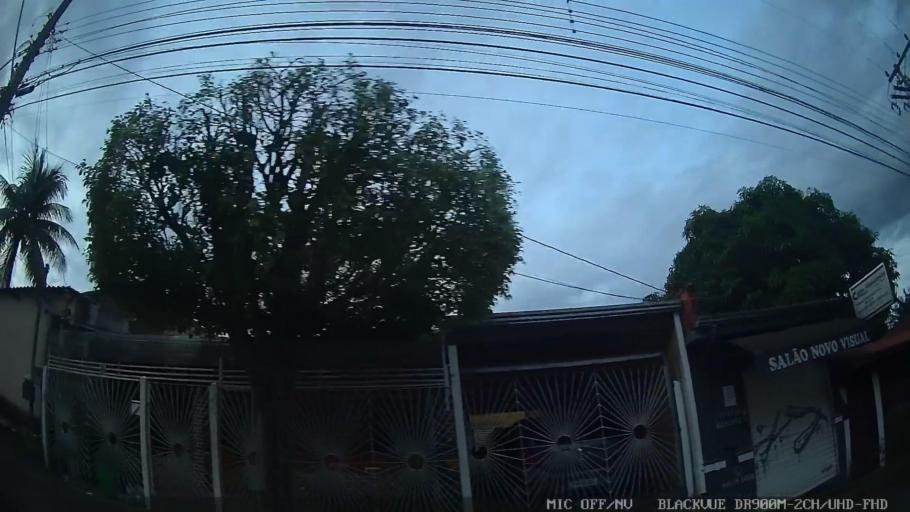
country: BR
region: Sao Paulo
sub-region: Indaiatuba
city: Indaiatuba
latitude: -23.1301
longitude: -47.2394
